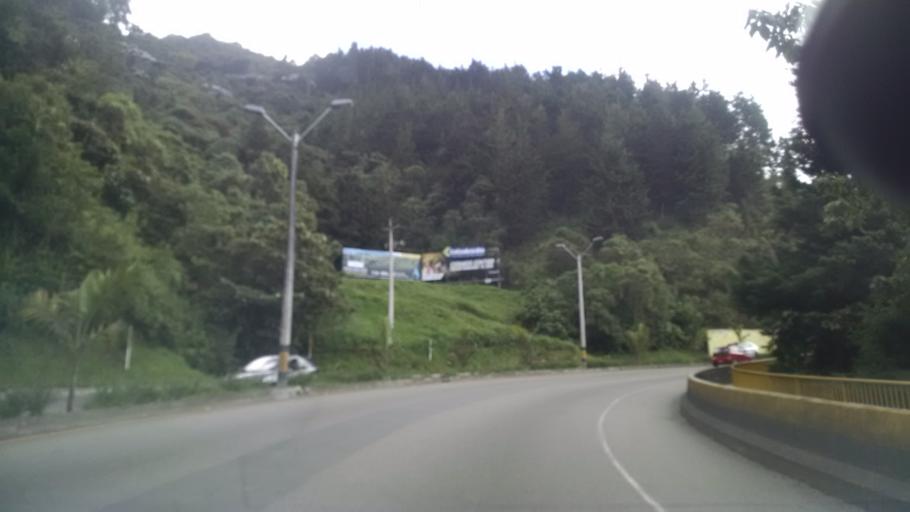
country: CO
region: Antioquia
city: Envigado
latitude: 6.1652
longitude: -75.5451
